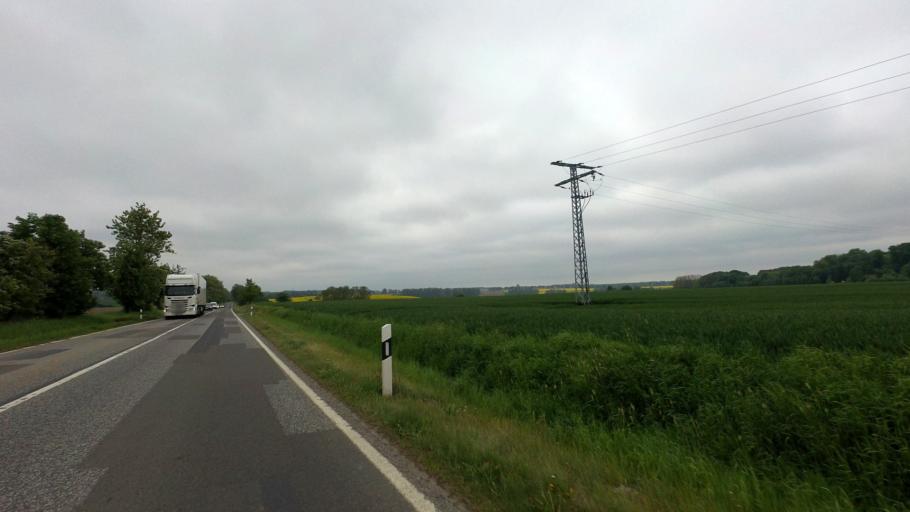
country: DE
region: Mecklenburg-Vorpommern
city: Mollenhagen
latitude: 53.5805
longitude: 12.8670
